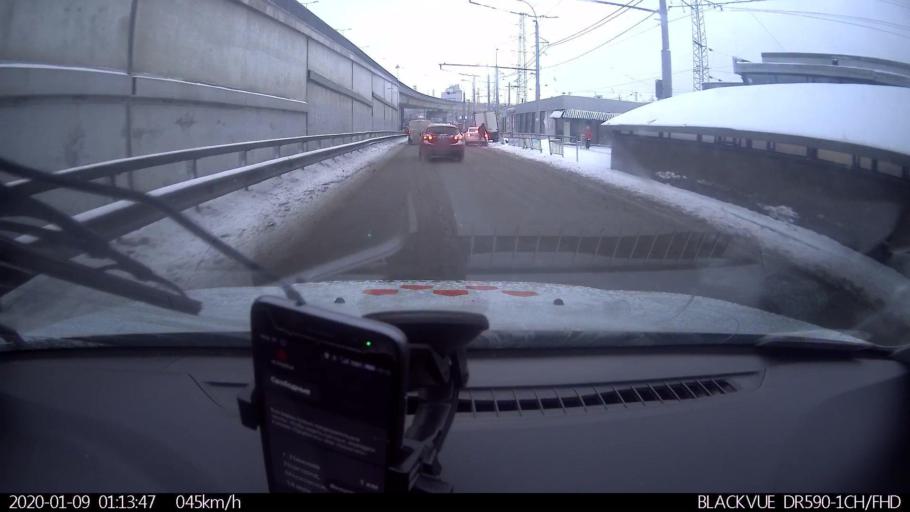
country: RU
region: Nizjnij Novgorod
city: Nizhniy Novgorod
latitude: 56.3270
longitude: 43.9451
